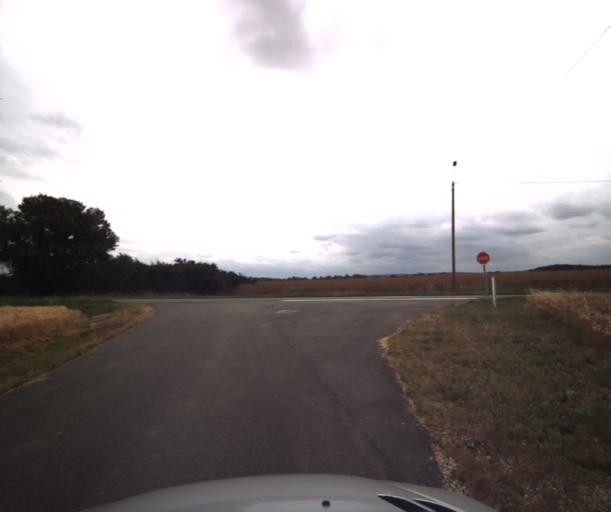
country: FR
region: Midi-Pyrenees
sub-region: Departement de la Haute-Garonne
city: Labarthe-sur-Leze
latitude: 43.4466
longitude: 1.4119
